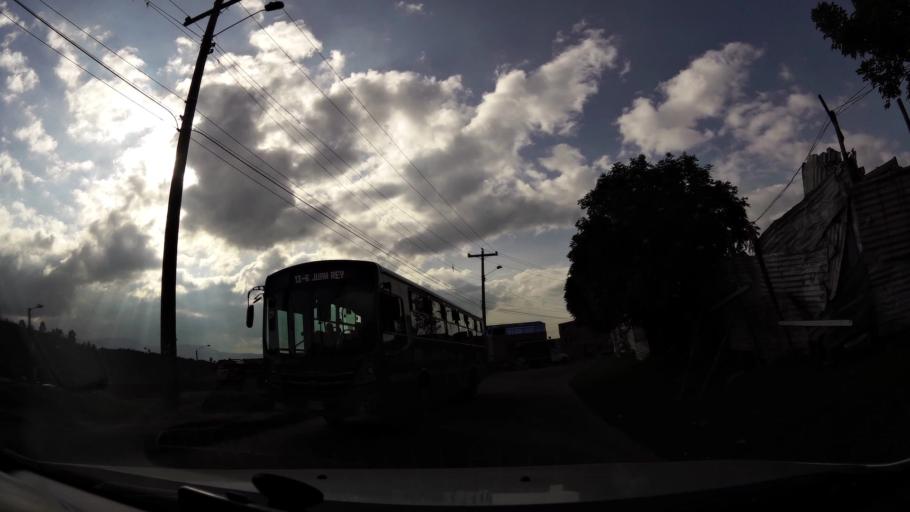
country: CO
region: Bogota D.C.
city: Bogota
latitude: 4.5364
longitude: -74.0912
